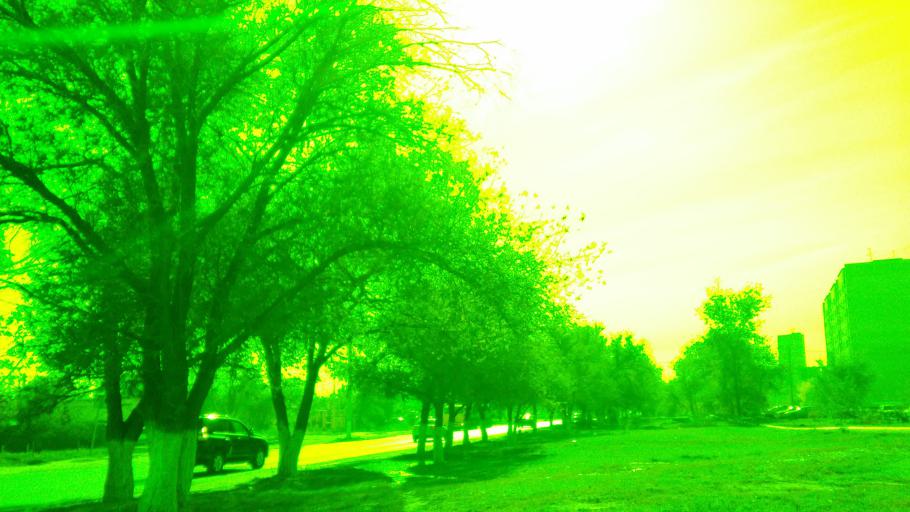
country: RU
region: Volgograd
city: Vodstroy
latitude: 48.8418
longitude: 44.6468
